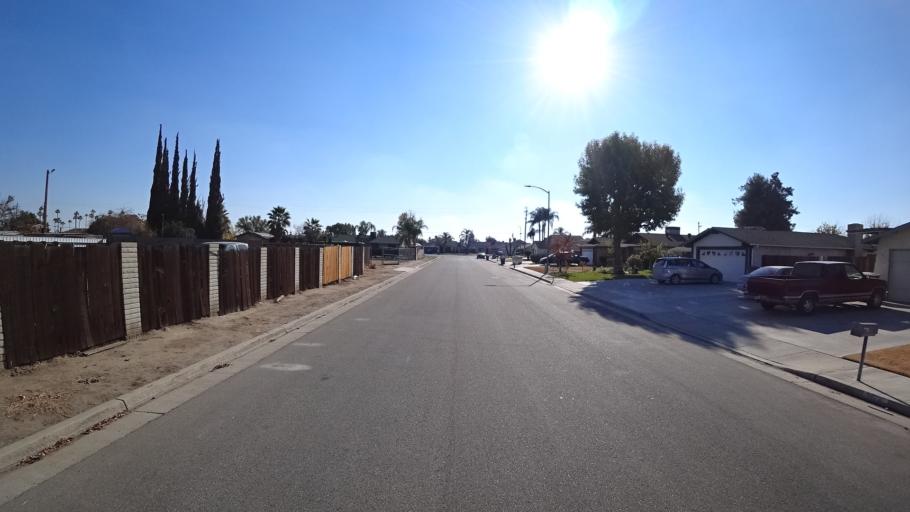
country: US
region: California
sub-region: Kern County
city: Greenfield
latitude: 35.3041
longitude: -119.0413
